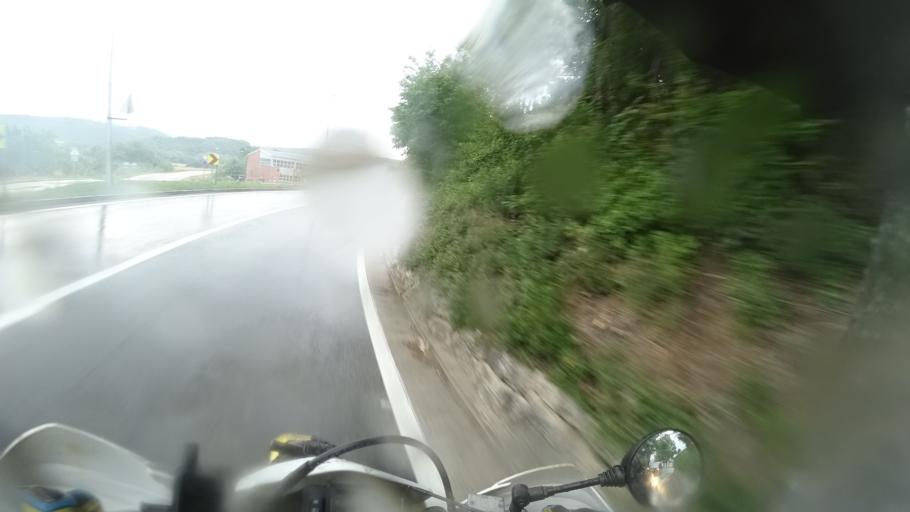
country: HR
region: Sibensko-Kniniska
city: Knin
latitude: 44.0393
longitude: 16.2075
